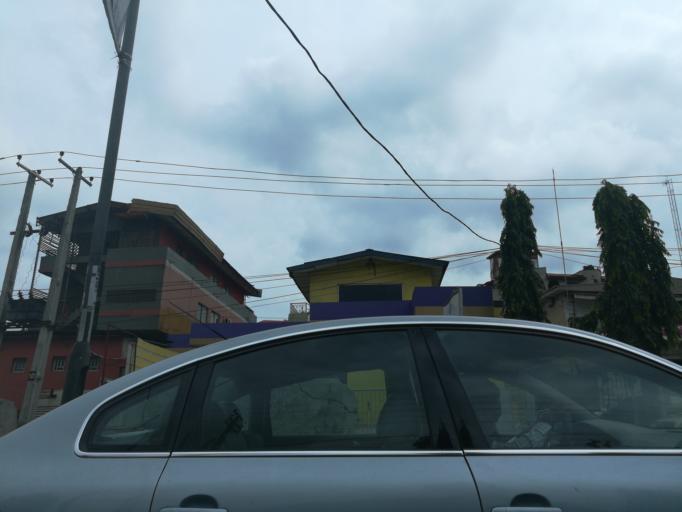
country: NG
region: Lagos
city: Ikeja
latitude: 6.6090
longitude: 3.3544
